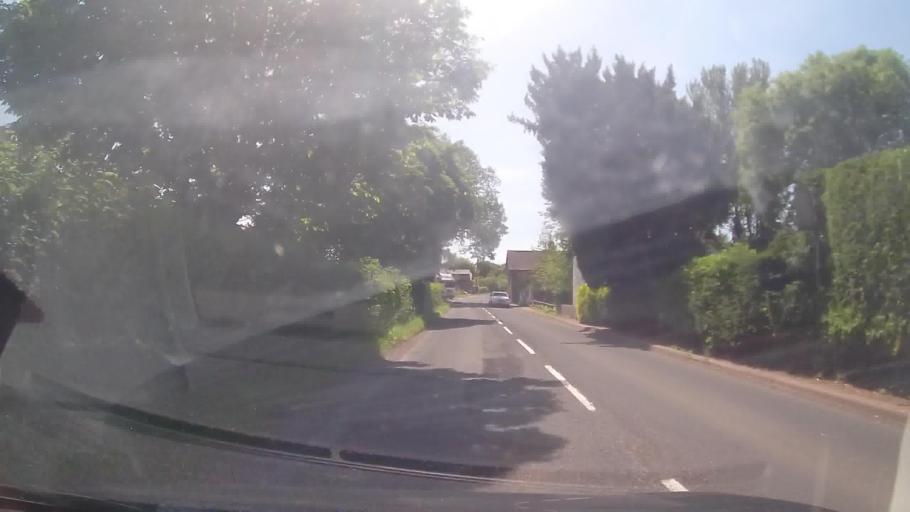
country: GB
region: England
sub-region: Herefordshire
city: Much Birch
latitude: 51.9676
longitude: -2.7404
